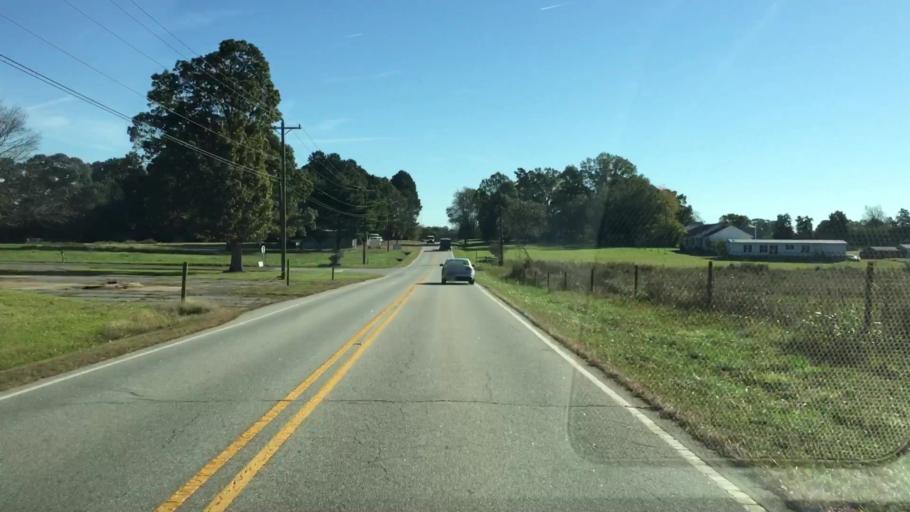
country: US
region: North Carolina
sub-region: Rowan County
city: Enochville
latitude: 35.6233
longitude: -80.6941
